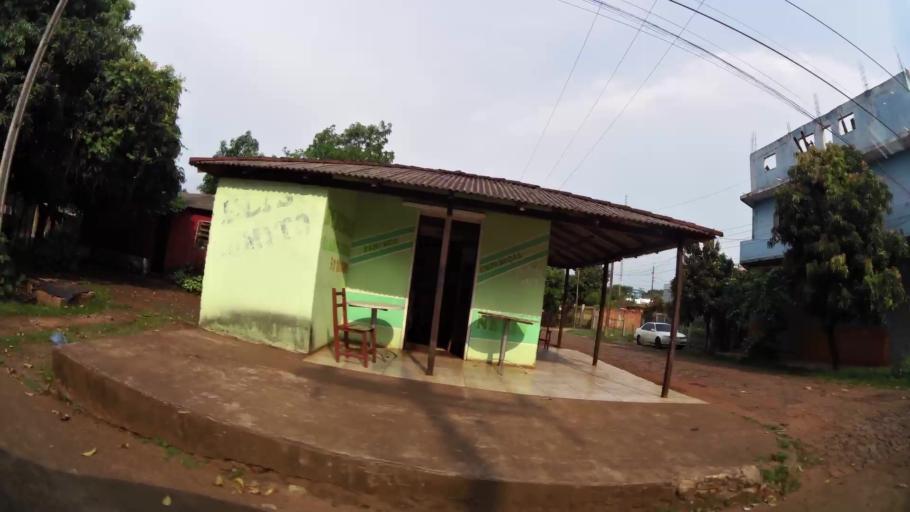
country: PY
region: Alto Parana
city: Ciudad del Este
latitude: -25.4978
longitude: -54.6598
